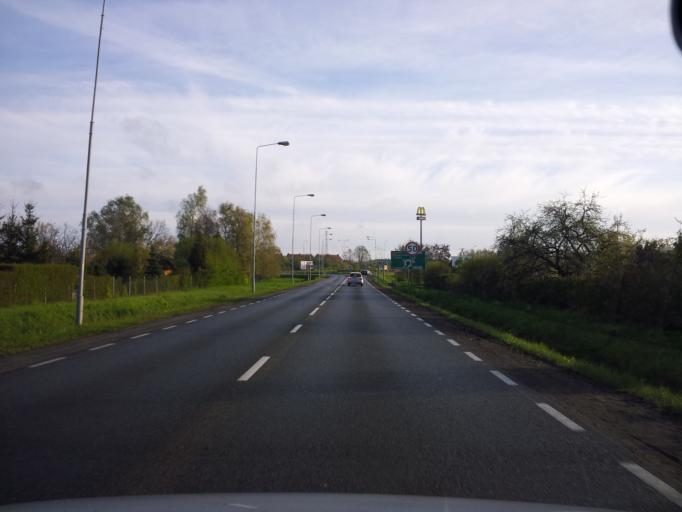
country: PL
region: Lubusz
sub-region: Powiat zarski
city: Zary
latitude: 51.6328
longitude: 15.1173
